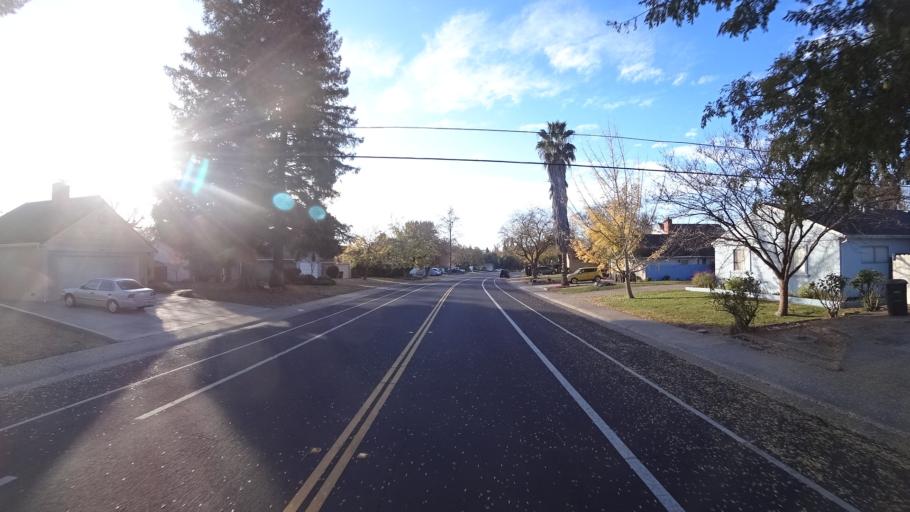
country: US
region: California
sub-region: Sacramento County
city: Citrus Heights
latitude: 38.6765
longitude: -121.3006
